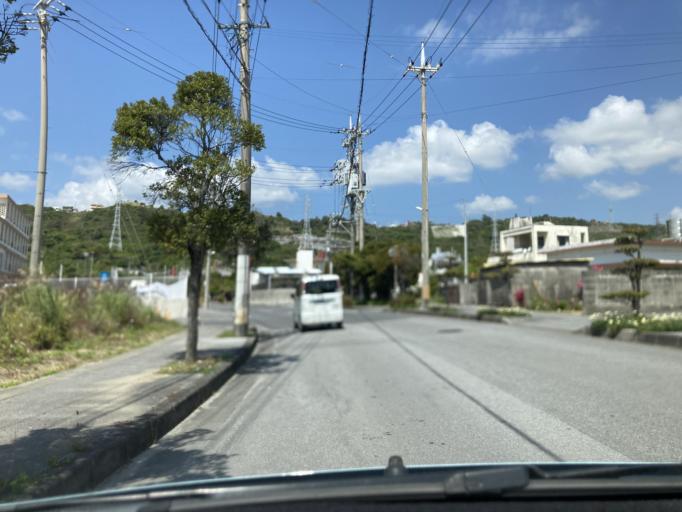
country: JP
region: Okinawa
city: Ginowan
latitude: 26.2618
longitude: 127.7908
